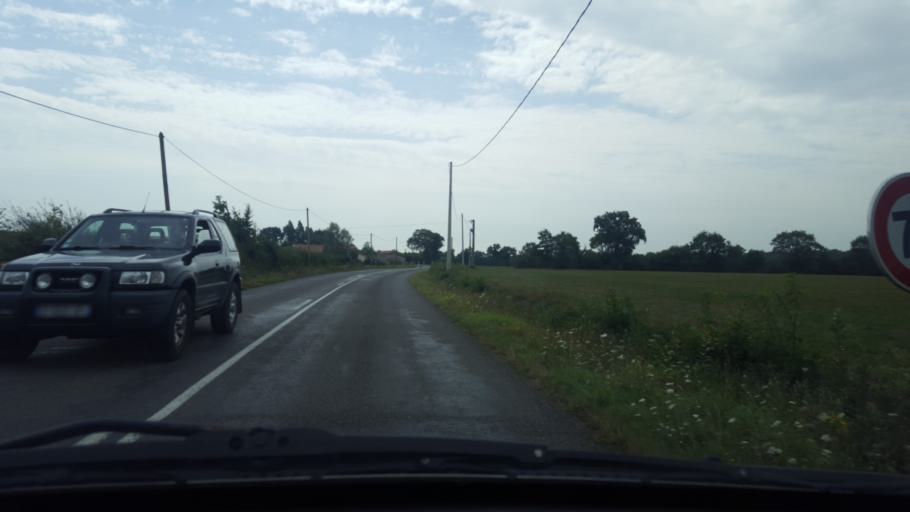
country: FR
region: Pays de la Loire
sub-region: Departement de la Loire-Atlantique
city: Touvois
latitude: 46.9192
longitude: -1.6829
